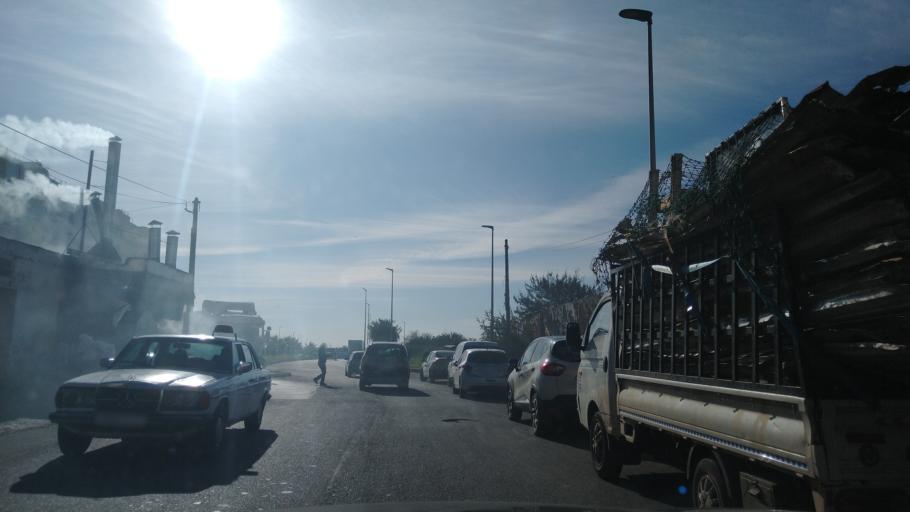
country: MA
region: Rabat-Sale-Zemmour-Zaer
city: Sale
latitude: 34.0034
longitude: -6.7472
